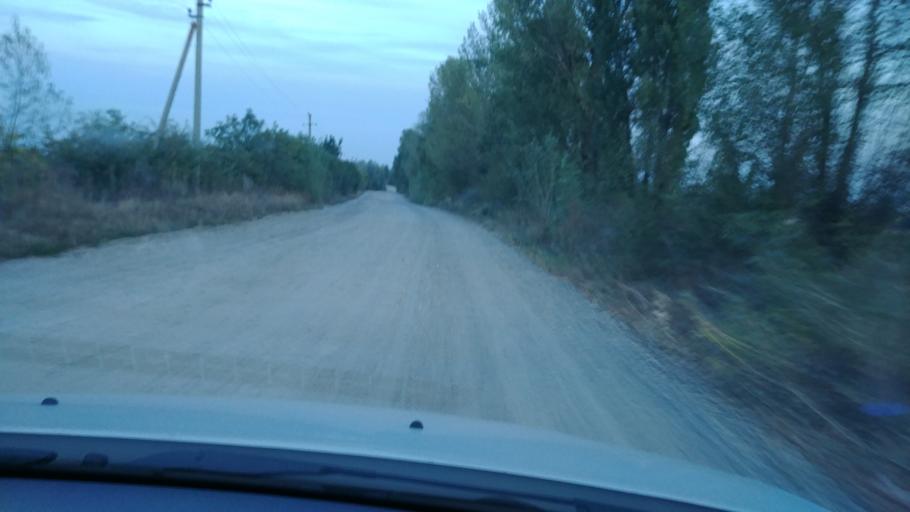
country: MD
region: Rezina
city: Saharna
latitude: 47.6796
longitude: 28.9188
